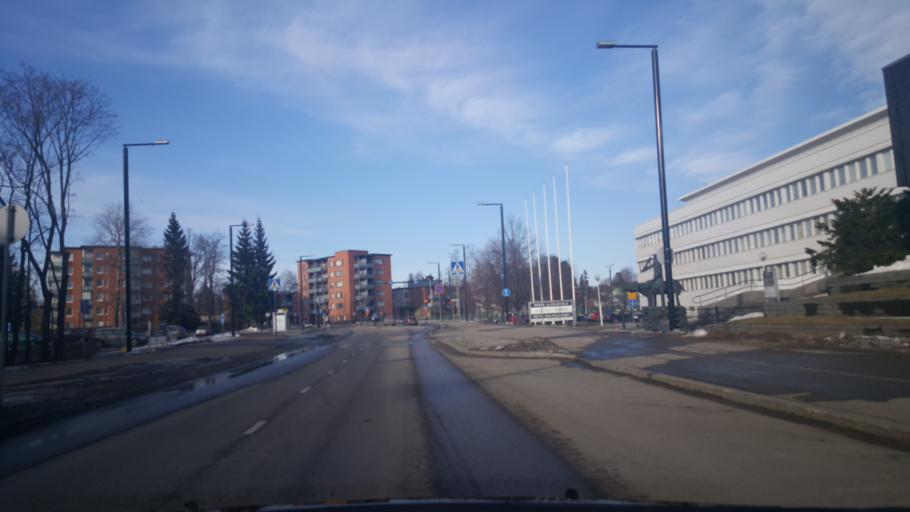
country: FI
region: Uusimaa
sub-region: Helsinki
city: Vantaa
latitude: 60.2983
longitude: 25.0406
